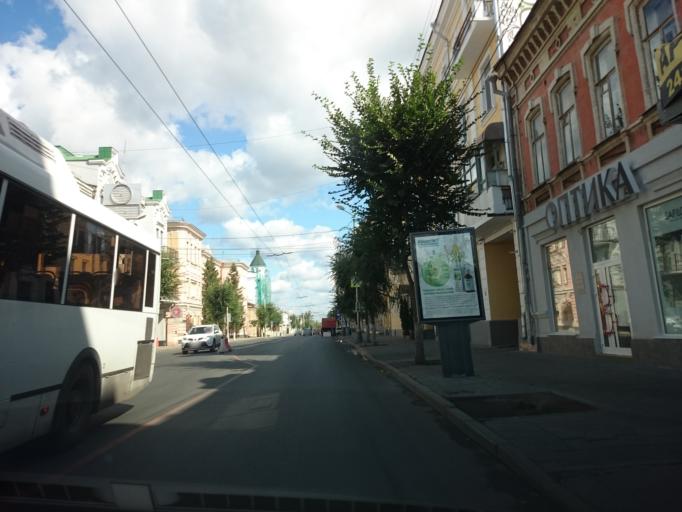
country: RU
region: Samara
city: Rozhdestveno
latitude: 53.1912
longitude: 50.0914
